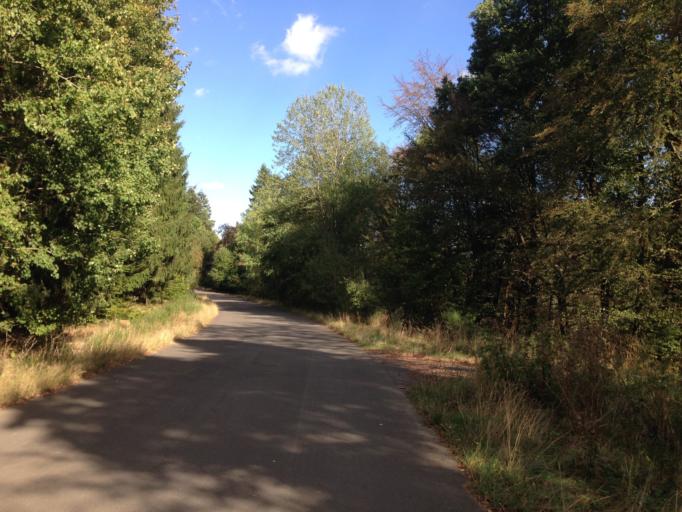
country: DE
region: Hesse
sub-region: Regierungsbezirk Giessen
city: Bad Endbach
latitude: 50.6680
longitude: 8.5463
